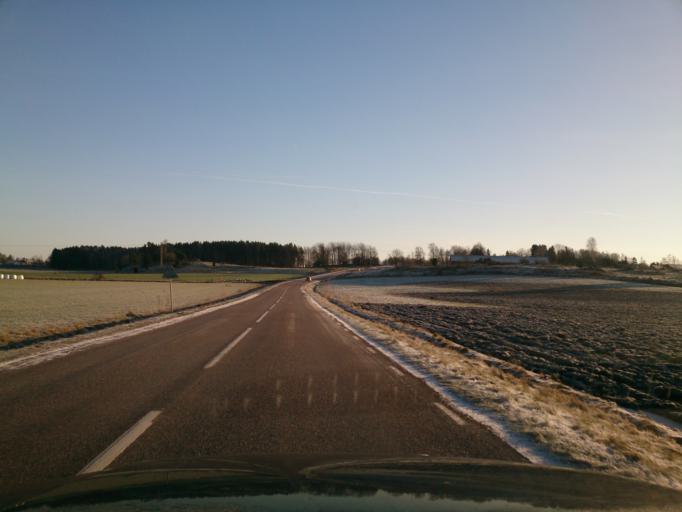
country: SE
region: OEstergoetland
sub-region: Linkopings Kommun
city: Linghem
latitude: 58.4320
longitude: 15.8990
